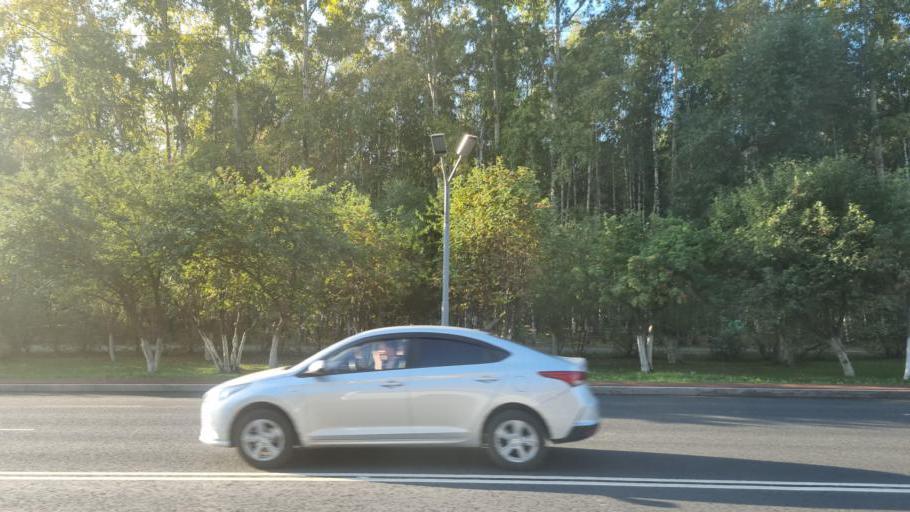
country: RU
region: Tomsk
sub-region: Tomskiy Rayon
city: Tomsk
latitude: 56.4552
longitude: 84.9562
